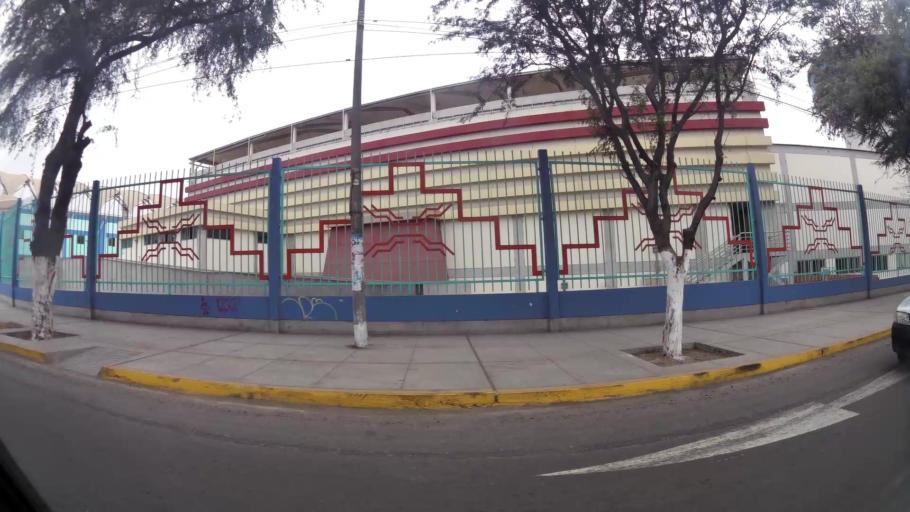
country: PE
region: La Libertad
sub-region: Provincia de Trujillo
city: Trujillo
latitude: -8.1181
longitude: -79.0176
